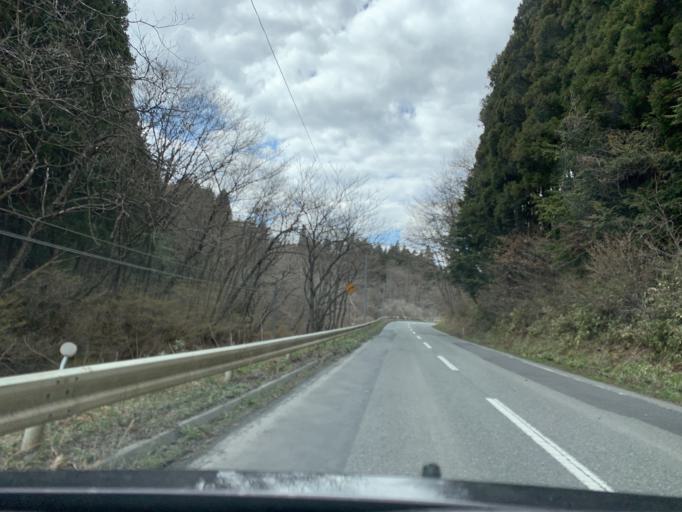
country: JP
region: Iwate
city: Ichinoseki
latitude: 38.8394
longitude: 141.3414
